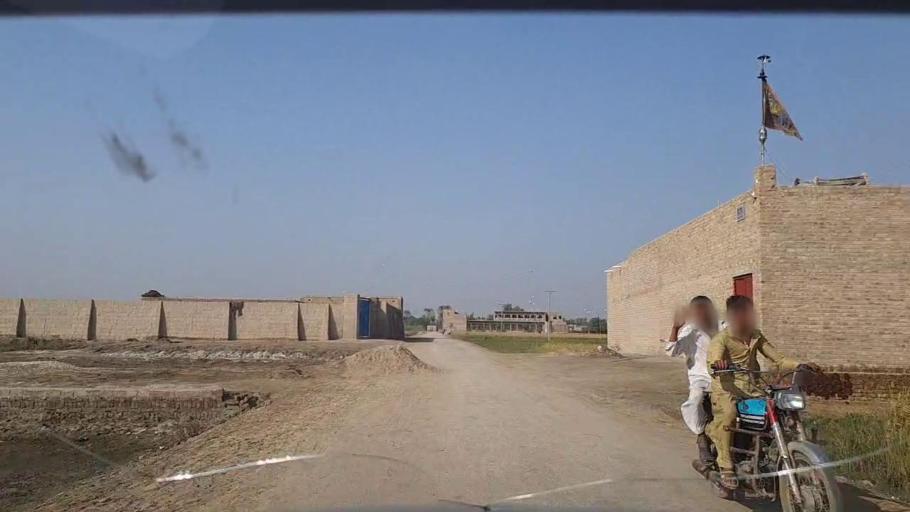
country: PK
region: Sindh
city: Shikarpur
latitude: 28.1172
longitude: 68.5789
